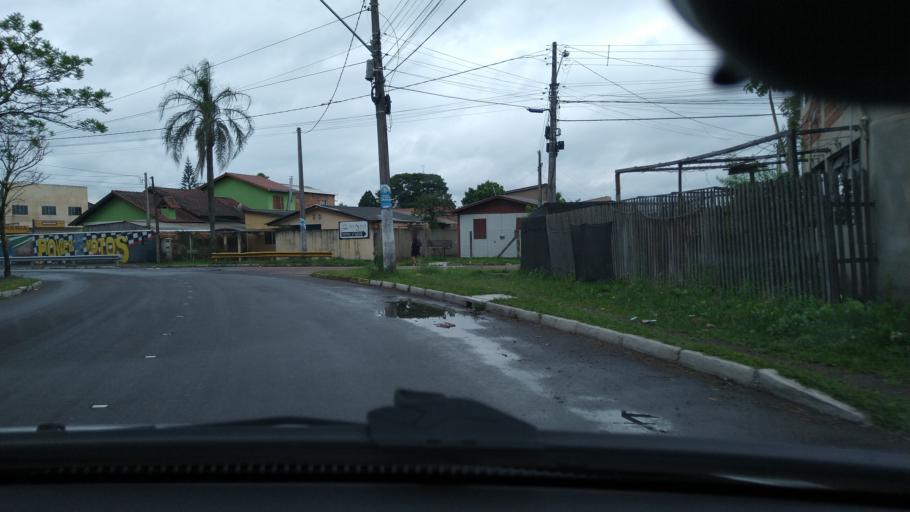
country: BR
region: Rio Grande do Sul
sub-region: Canoas
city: Canoas
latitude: -29.9019
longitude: -51.2169
